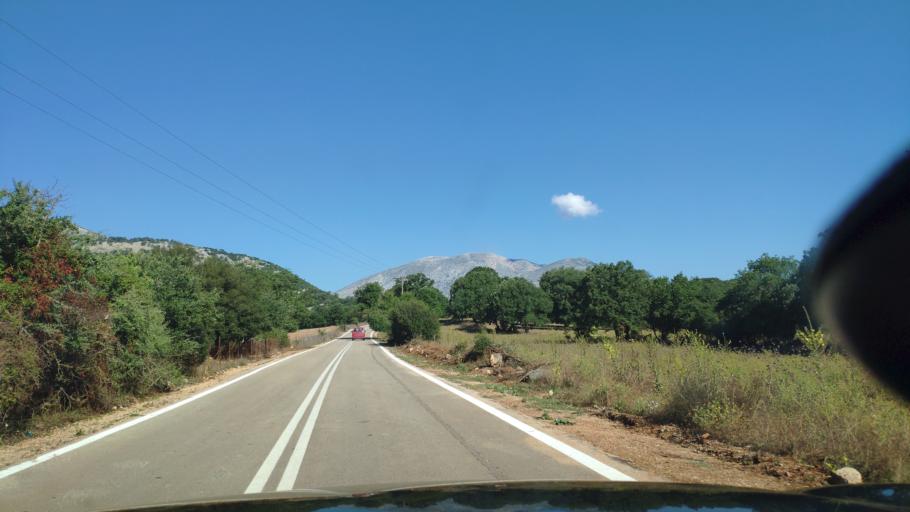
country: GR
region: West Greece
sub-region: Nomos Aitolias kai Akarnanias
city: Fitiai
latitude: 38.6851
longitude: 21.1212
